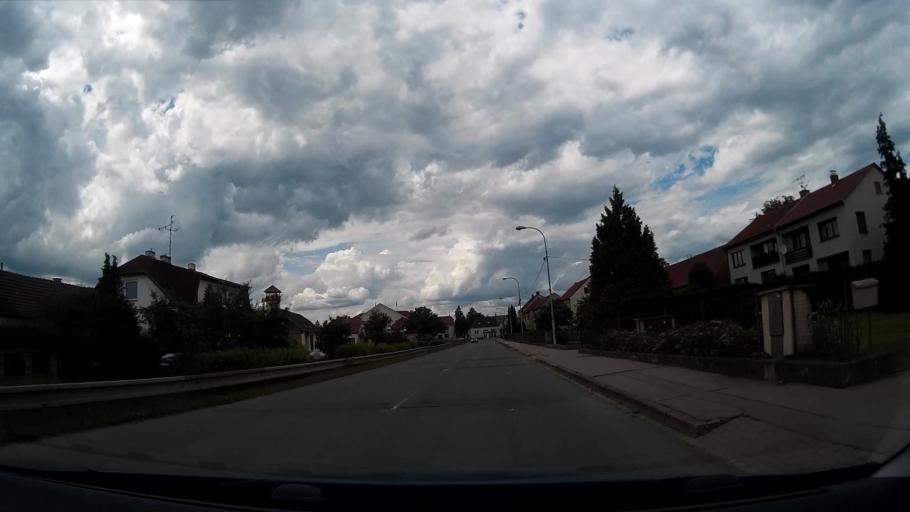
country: CZ
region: South Moravian
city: Strelice
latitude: 49.1525
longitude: 16.5068
